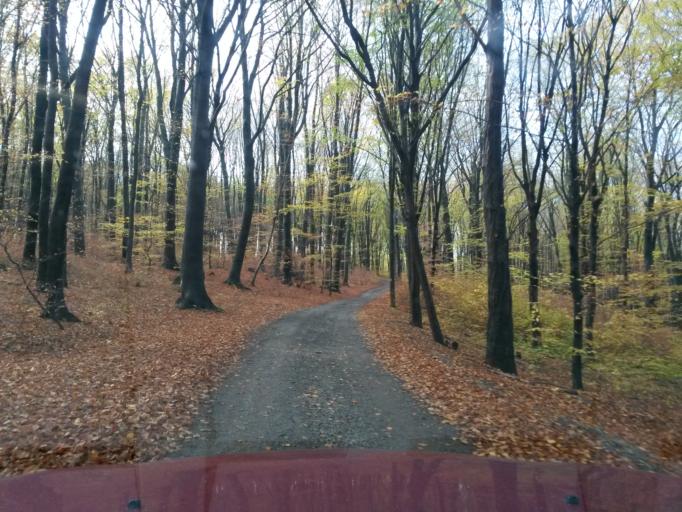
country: SK
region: Kosicky
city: Kosice
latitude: 48.7584
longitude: 21.2185
